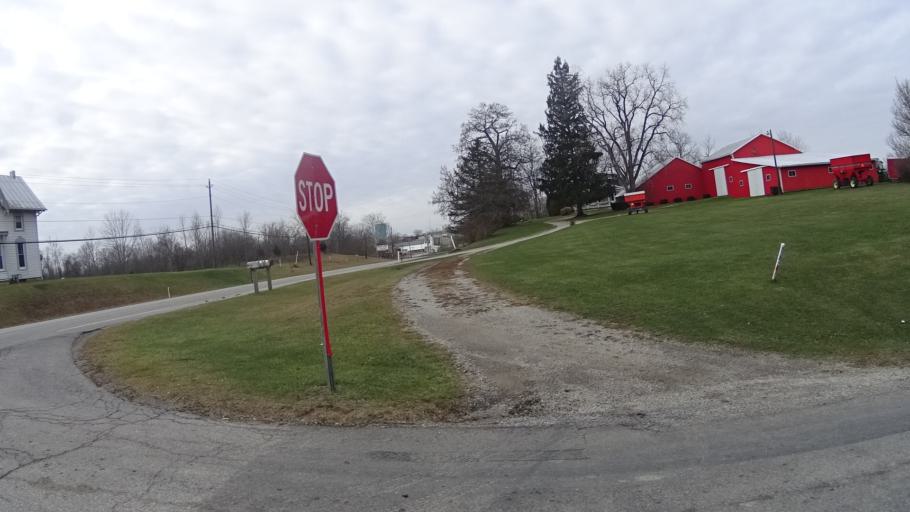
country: US
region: Ohio
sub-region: Lorain County
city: Wellington
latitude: 41.1691
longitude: -82.2430
